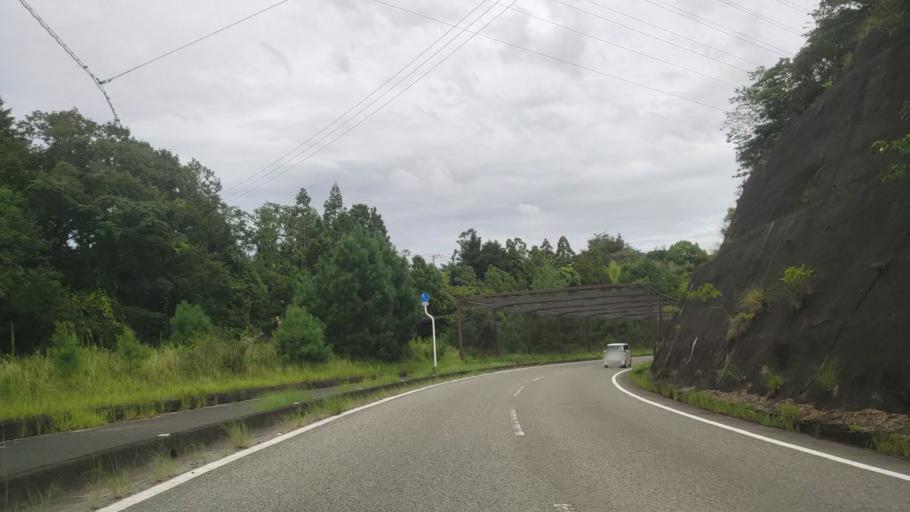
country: JP
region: Wakayama
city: Tanabe
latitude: 33.6848
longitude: 135.3870
